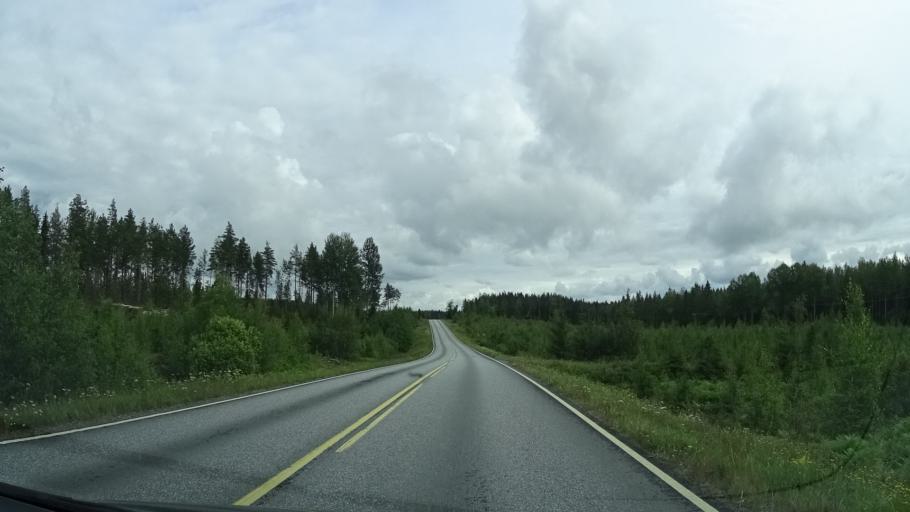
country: FI
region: Haeme
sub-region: Forssa
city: Humppila
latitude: 61.0967
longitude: 23.3497
